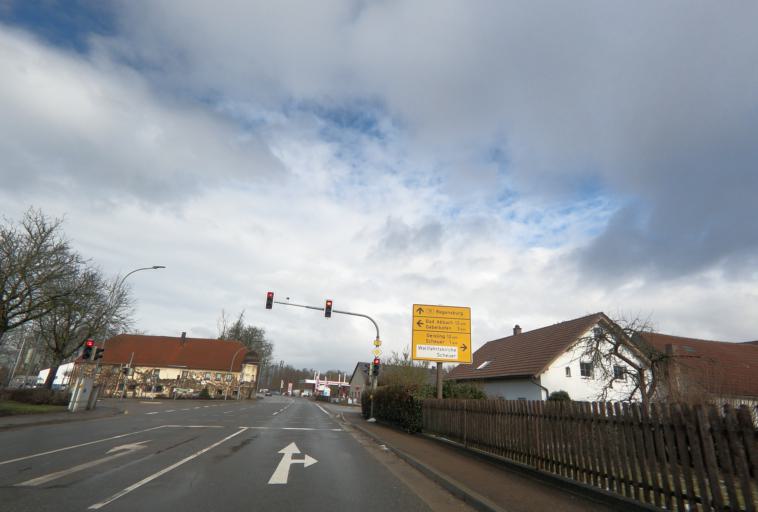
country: DE
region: Bavaria
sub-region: Upper Palatinate
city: Kofering
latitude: 48.9390
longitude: 12.2016
